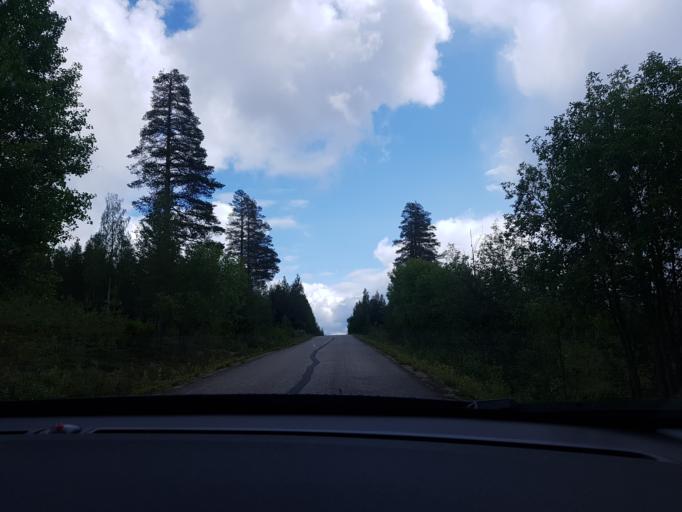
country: FI
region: Kainuu
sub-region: Kehys-Kainuu
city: Kuhmo
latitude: 64.4605
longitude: 29.6170
